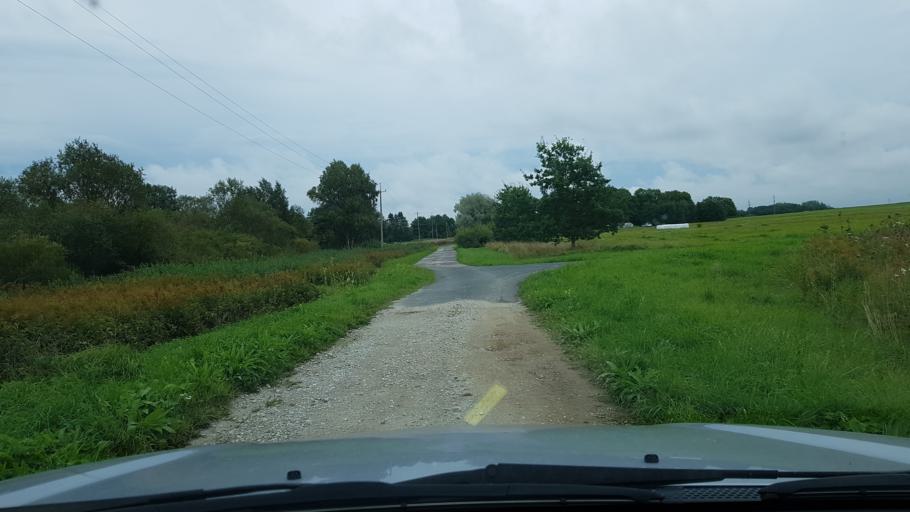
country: EE
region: Harju
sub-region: Joelaehtme vald
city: Loo
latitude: 59.4132
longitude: 24.9561
